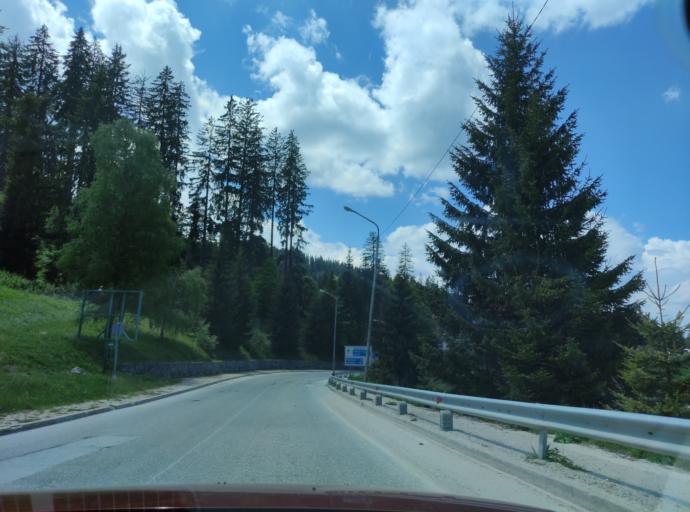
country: BG
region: Smolyan
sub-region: Obshtina Smolyan
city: Smolyan
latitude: 41.6511
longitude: 24.6983
